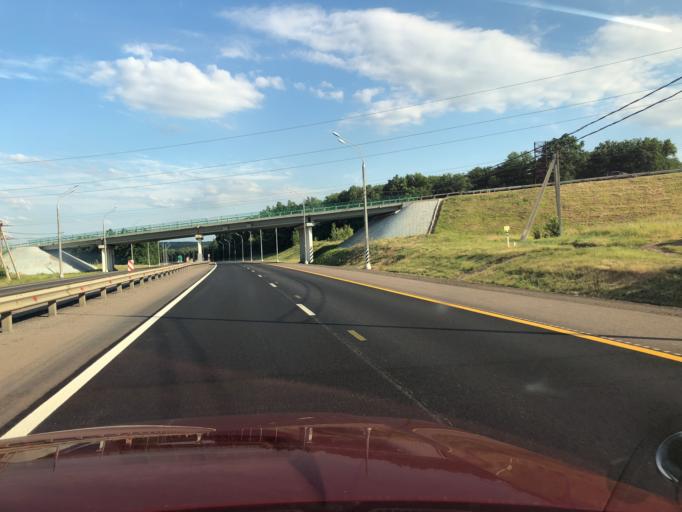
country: RU
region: Lipetsk
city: Zadonsk
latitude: 52.3868
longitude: 38.8676
